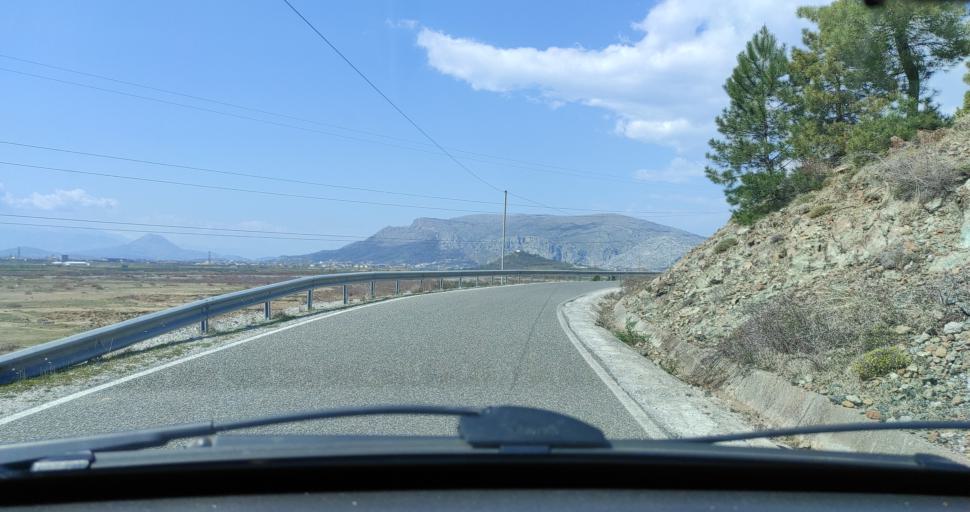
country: AL
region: Shkoder
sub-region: Rrethi i Shkodres
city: Vau i Dejes
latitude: 41.9852
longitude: 19.6439
